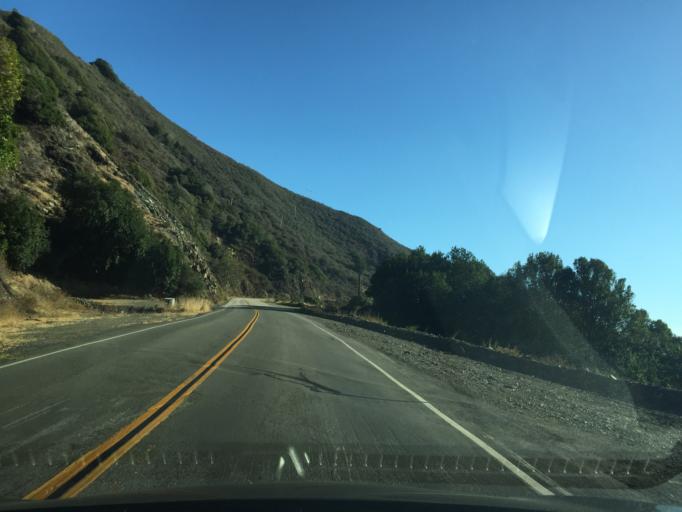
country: US
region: California
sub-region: San Luis Obispo County
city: Cambria
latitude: 35.8138
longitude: -121.3589
